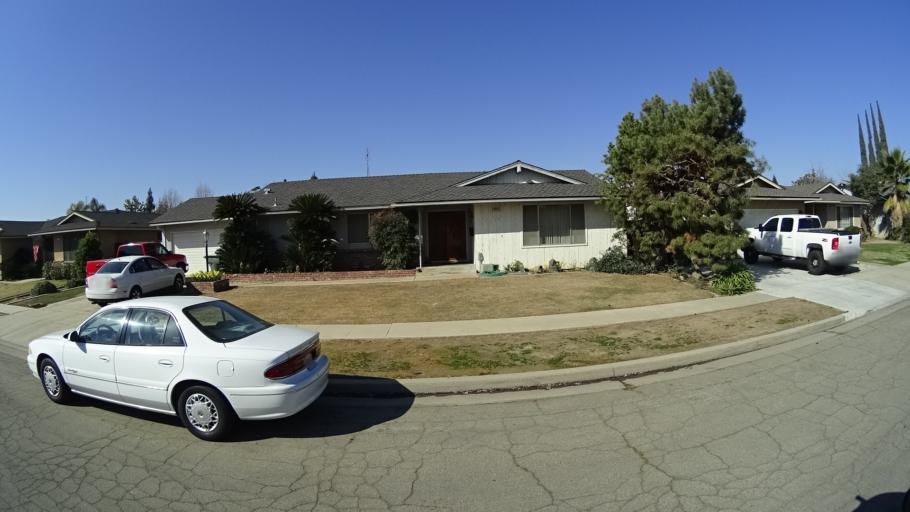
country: US
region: California
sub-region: Fresno County
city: Clovis
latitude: 36.8311
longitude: -119.7414
